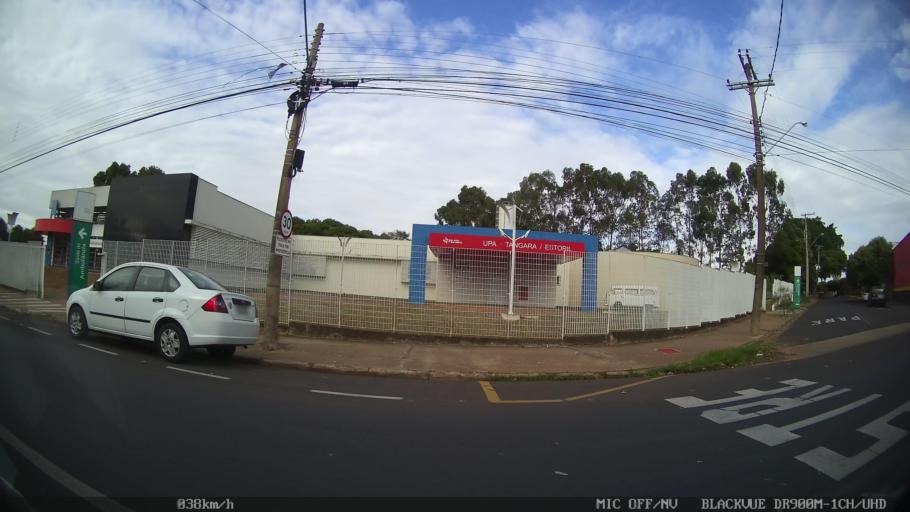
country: BR
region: Sao Paulo
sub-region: Sao Jose Do Rio Preto
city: Sao Jose do Rio Preto
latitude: -20.8396
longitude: -49.3750
